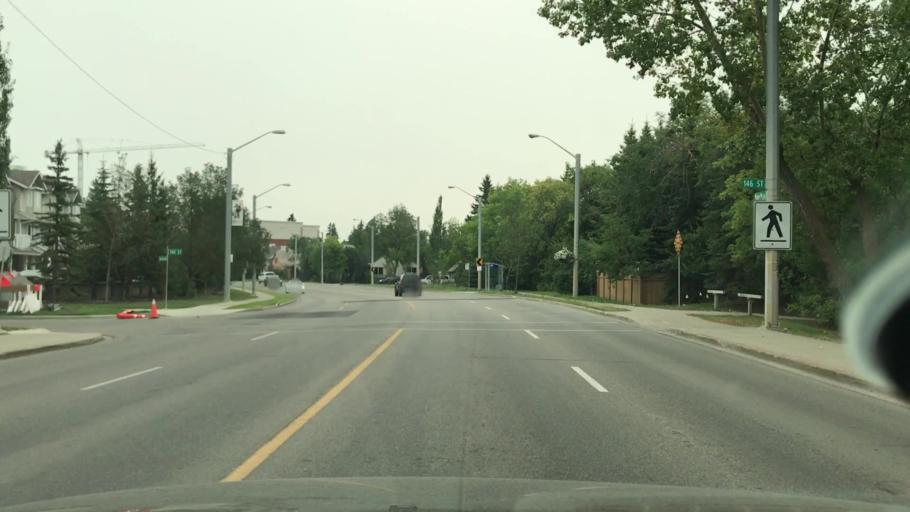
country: CA
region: Alberta
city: Edmonton
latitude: 53.5420
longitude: -113.5730
